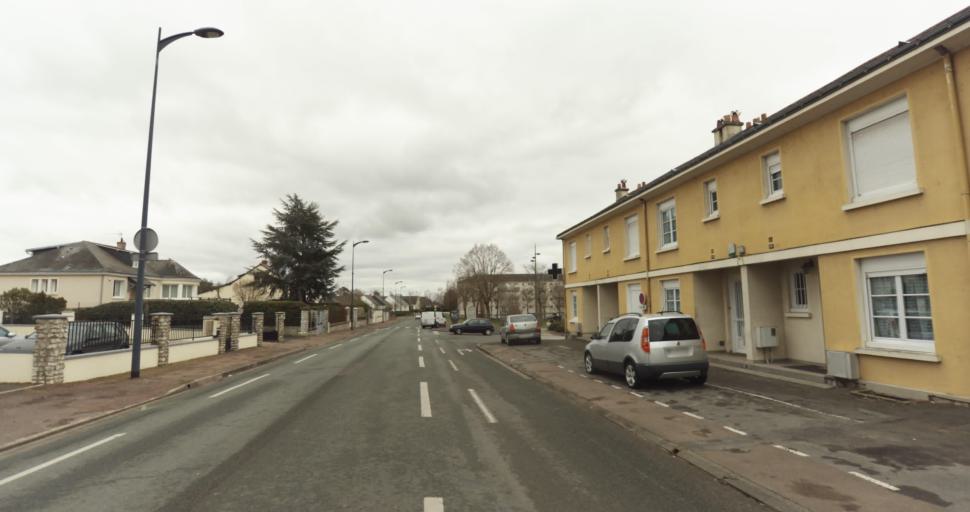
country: FR
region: Pays de la Loire
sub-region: Departement de Maine-et-Loire
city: Saumur
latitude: 47.2519
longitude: -0.0680
